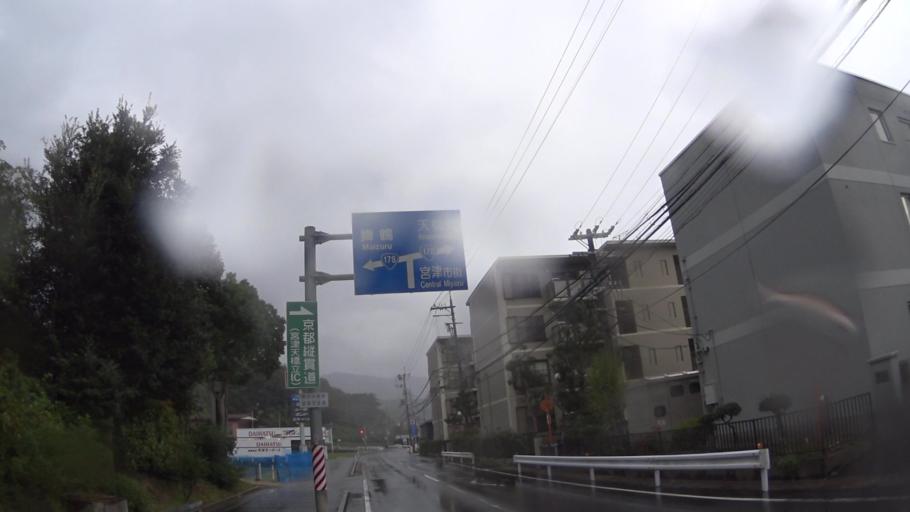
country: JP
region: Kyoto
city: Miyazu
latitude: 35.5494
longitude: 135.2114
